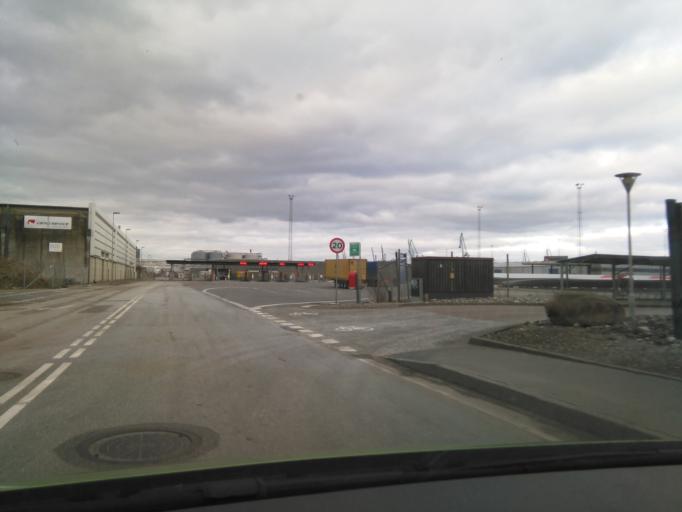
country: DK
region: Central Jutland
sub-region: Arhus Kommune
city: Arhus
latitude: 56.1422
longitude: 10.2119
